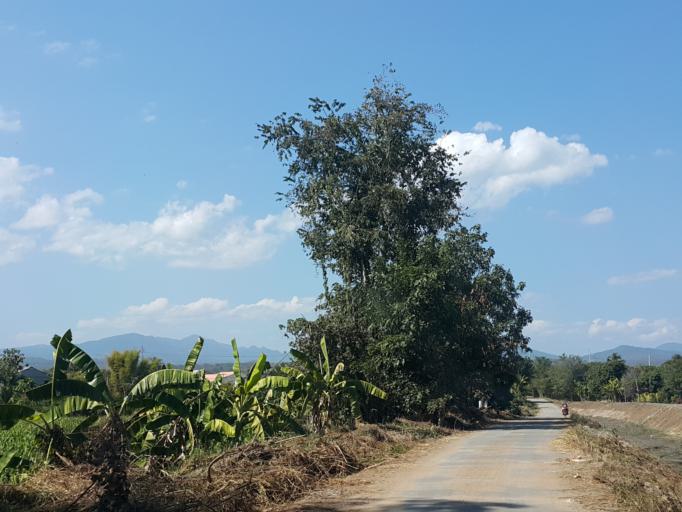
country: TH
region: Chiang Mai
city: Mae Taeng
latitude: 19.0996
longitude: 98.9388
